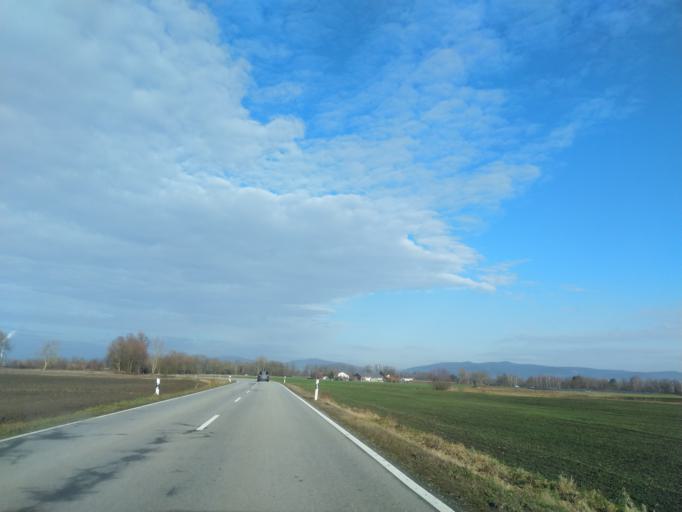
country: DE
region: Bavaria
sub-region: Lower Bavaria
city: Aholming
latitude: 48.7506
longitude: 12.9052
